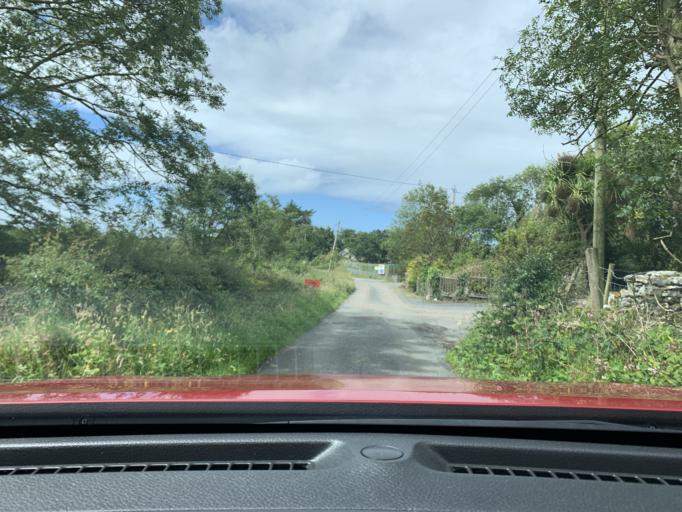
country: IE
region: Connaught
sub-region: Sligo
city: Sligo
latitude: 54.3823
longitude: -8.5117
